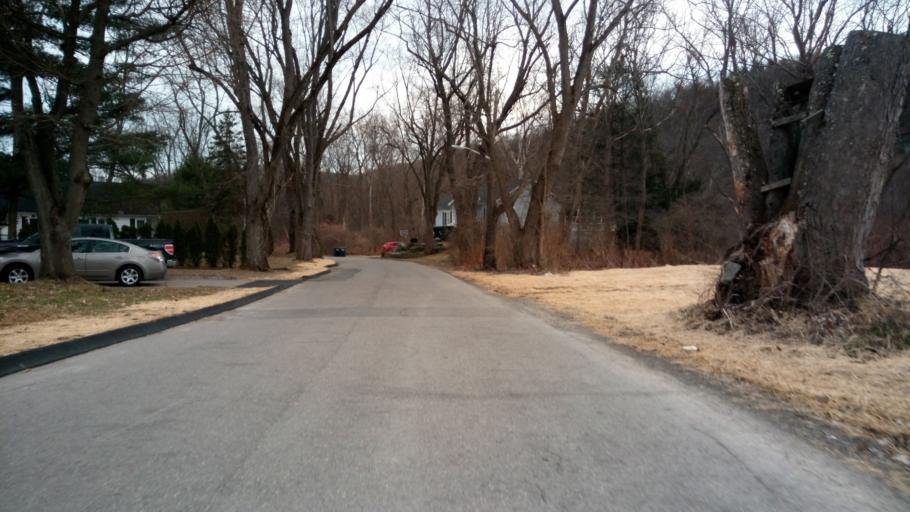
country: US
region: New York
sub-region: Chemung County
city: West Elmira
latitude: 42.0790
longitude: -76.8594
